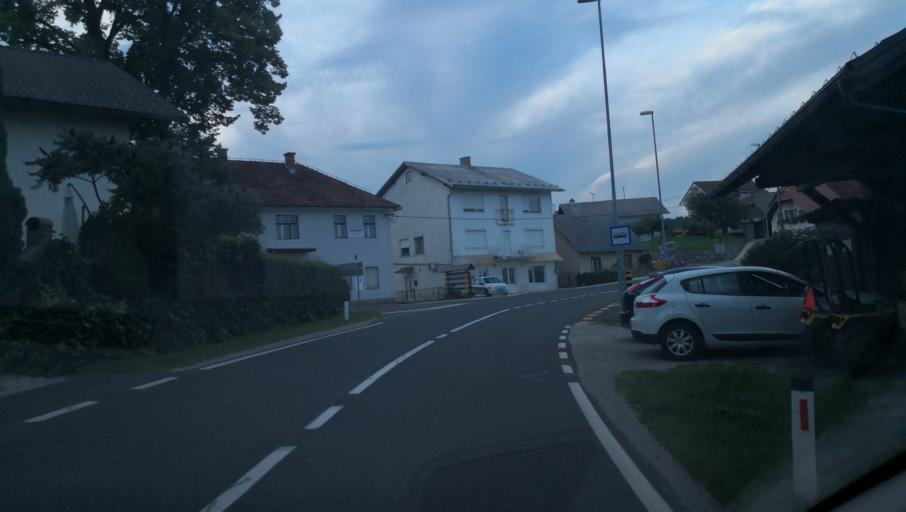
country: SI
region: Metlika
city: Metlika
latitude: 45.6893
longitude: 15.2732
